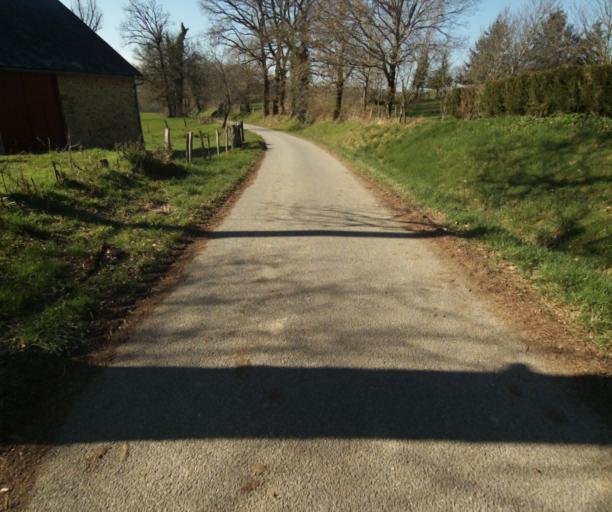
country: FR
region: Limousin
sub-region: Departement de la Correze
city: Chamboulive
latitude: 45.4804
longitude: 1.6887
